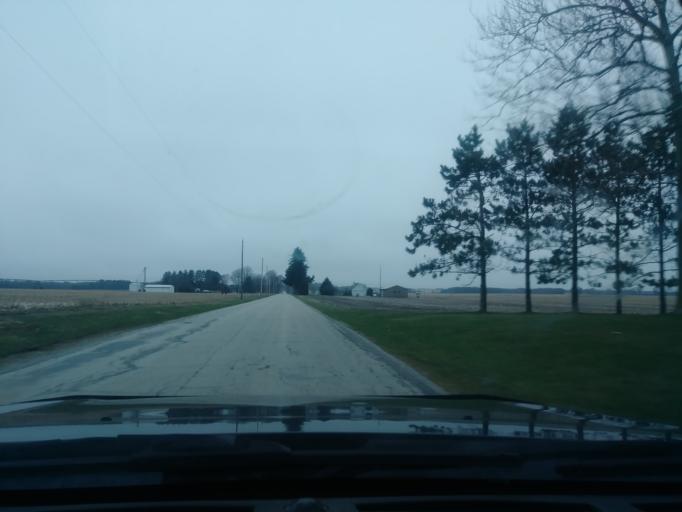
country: US
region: Indiana
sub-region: LaPorte County
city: LaPorte
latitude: 41.5776
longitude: -86.7981
